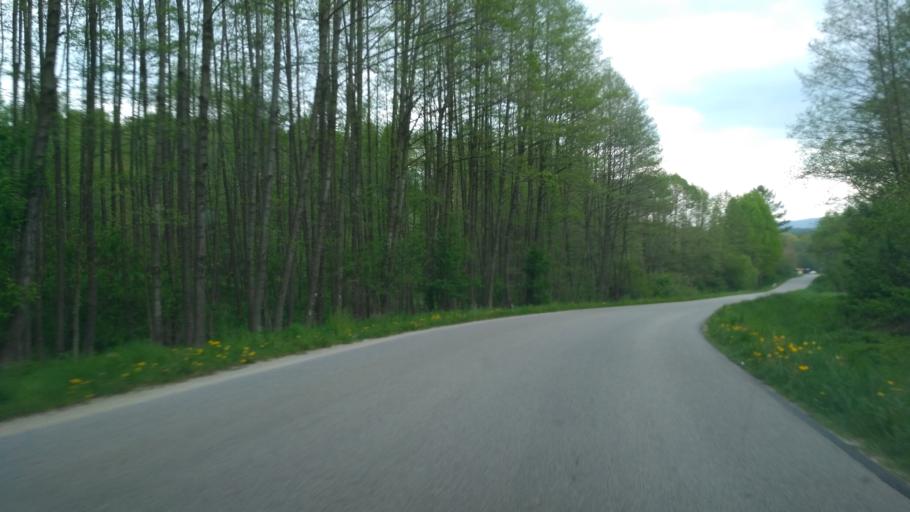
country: PL
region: Subcarpathian Voivodeship
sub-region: Powiat debicki
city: Leki Gorne
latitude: 49.9816
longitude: 21.1557
